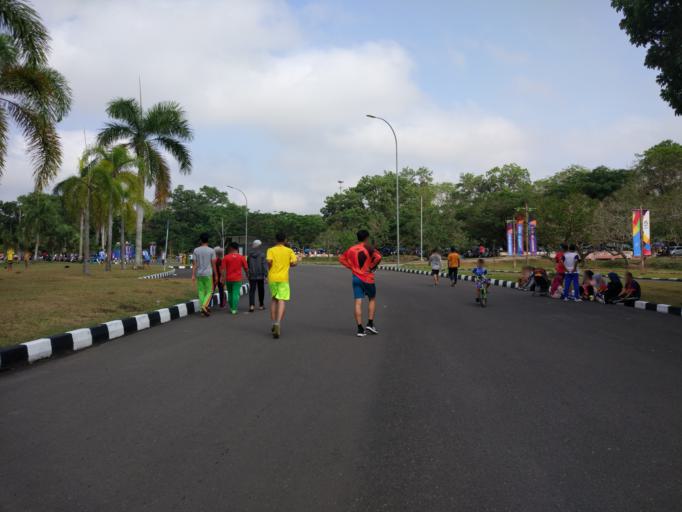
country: ID
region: South Sumatra
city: Plaju
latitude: -3.0205
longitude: 104.7898
